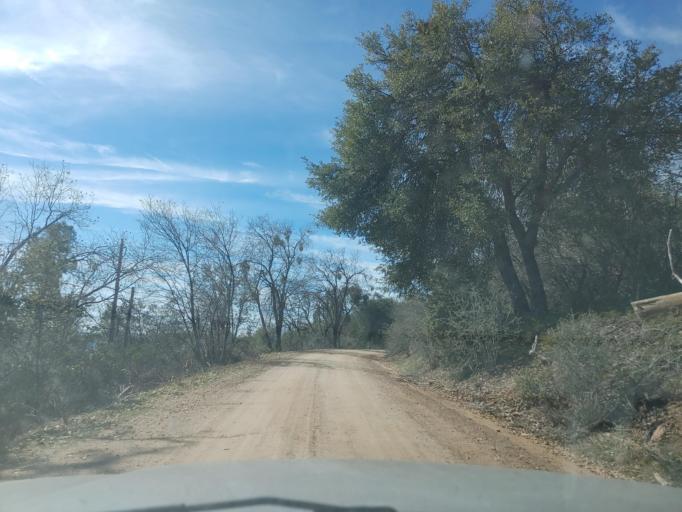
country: US
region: California
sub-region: Madera County
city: Ahwahnee
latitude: 37.4166
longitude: -119.6910
